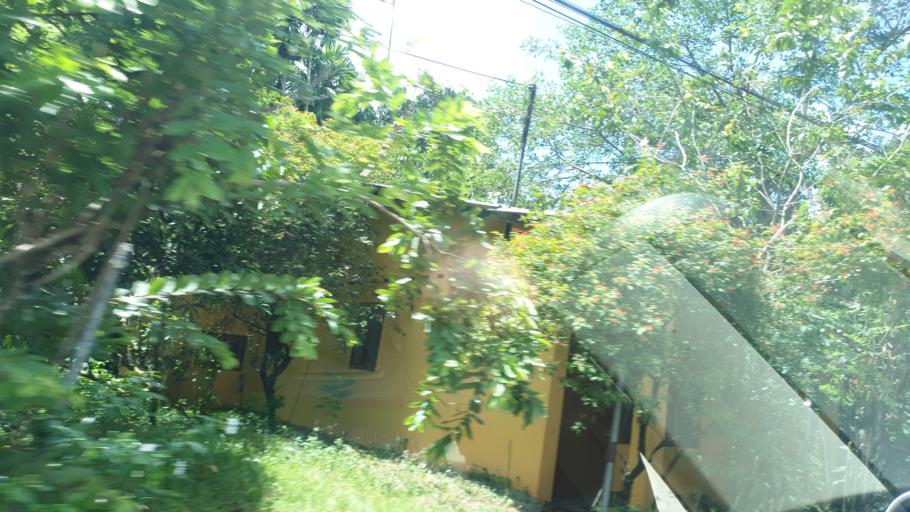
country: LK
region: Western
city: Horawala Junction
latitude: 6.5213
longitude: 80.2198
